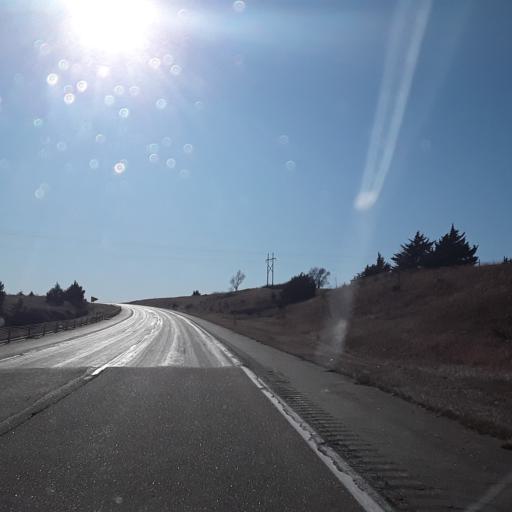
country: US
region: Nebraska
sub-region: Frontier County
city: Stockville
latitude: 40.5421
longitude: -100.6464
